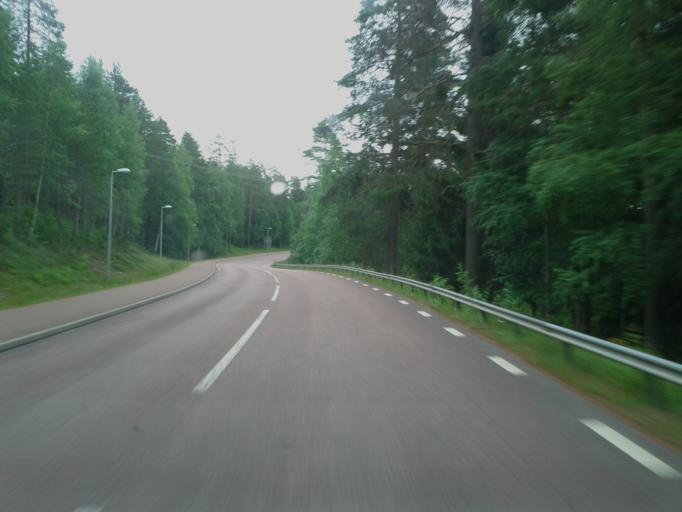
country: SE
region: Dalarna
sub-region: Alvdalens Kommun
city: AElvdalen
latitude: 61.2427
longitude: 14.0318
